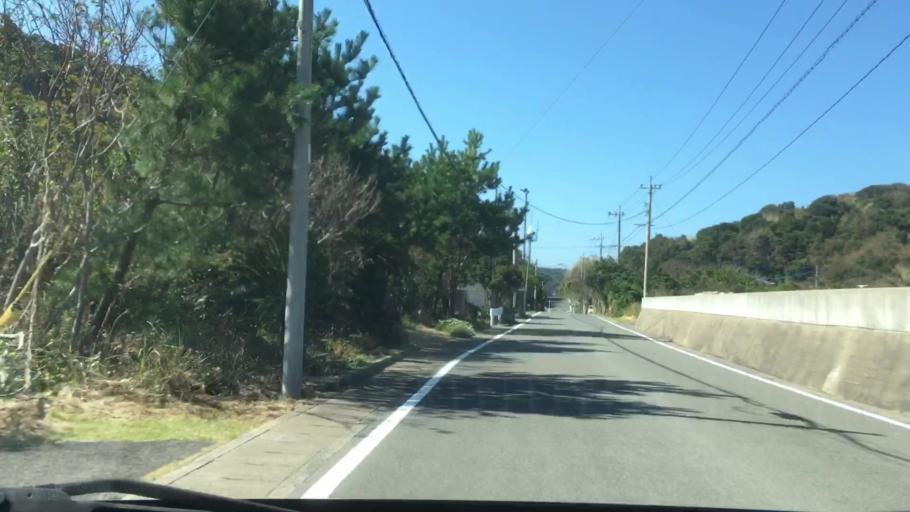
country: JP
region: Nagasaki
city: Sasebo
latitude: 33.0080
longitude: 129.5603
